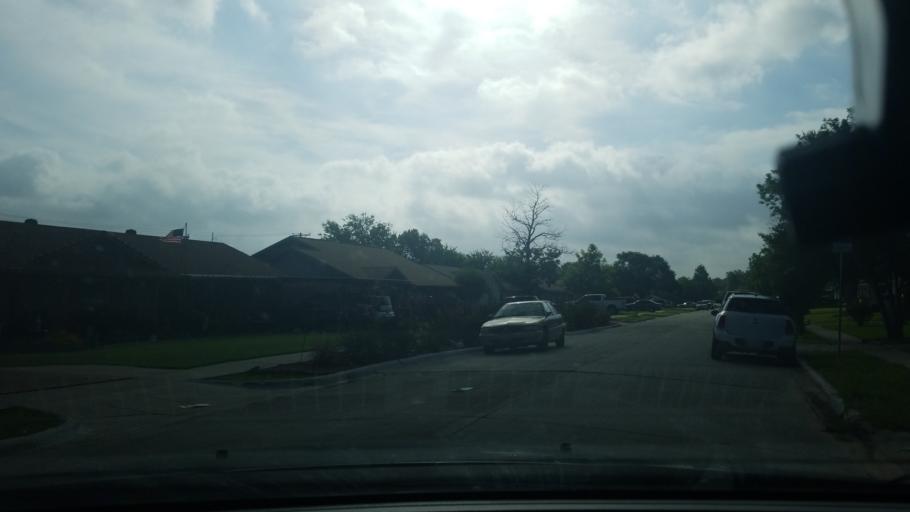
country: US
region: Texas
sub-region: Dallas County
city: Mesquite
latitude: 32.7745
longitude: -96.6427
